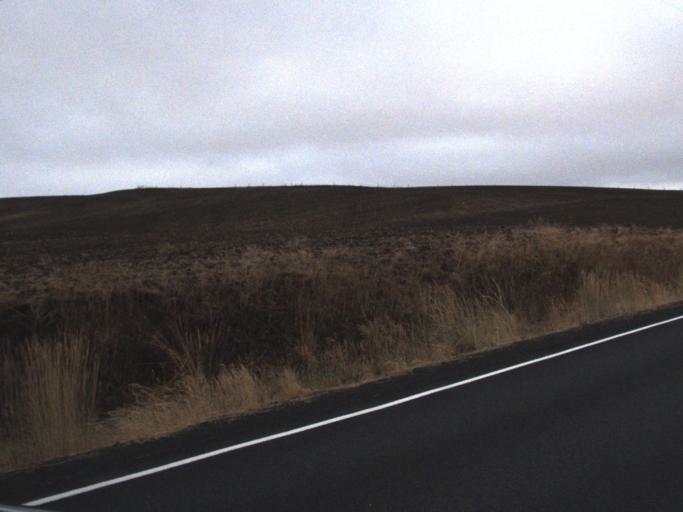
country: US
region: Washington
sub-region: Spokane County
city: Medical Lake
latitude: 47.7116
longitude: -117.8730
